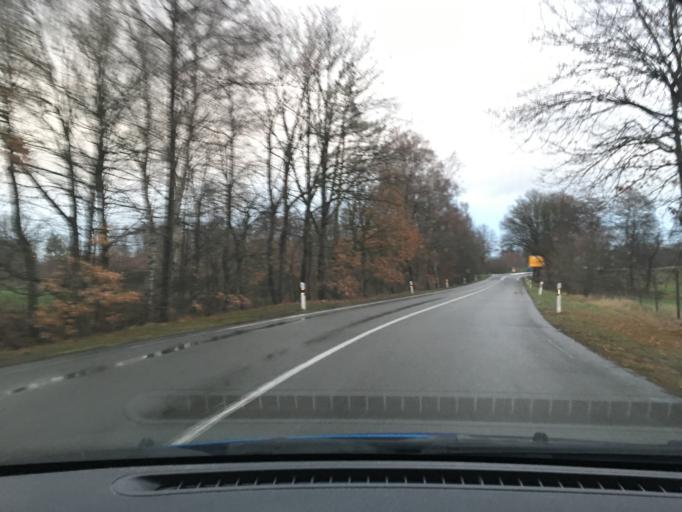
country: DE
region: Lower Saxony
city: Bad Fallingbostel
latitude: 52.8906
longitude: 9.7650
